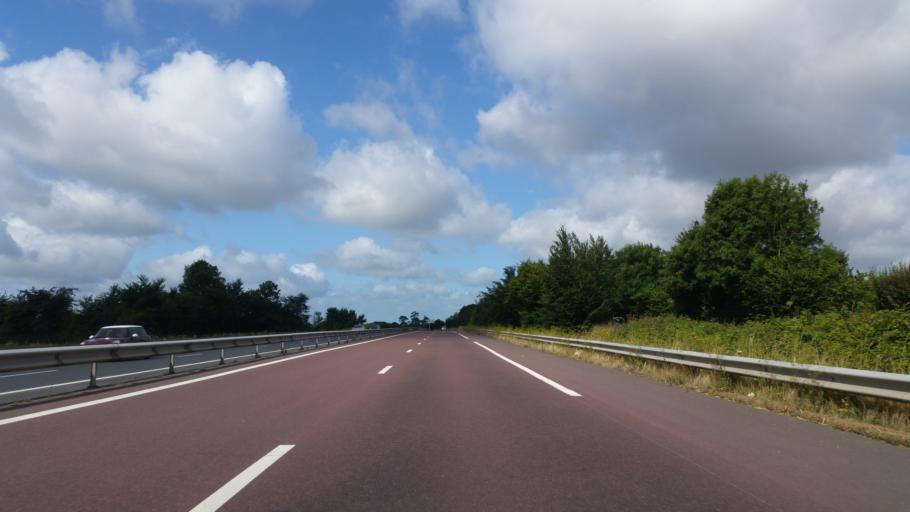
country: FR
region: Lower Normandy
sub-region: Departement du Calvados
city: Grandcamp-Maisy
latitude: 49.3426
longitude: -1.0441
